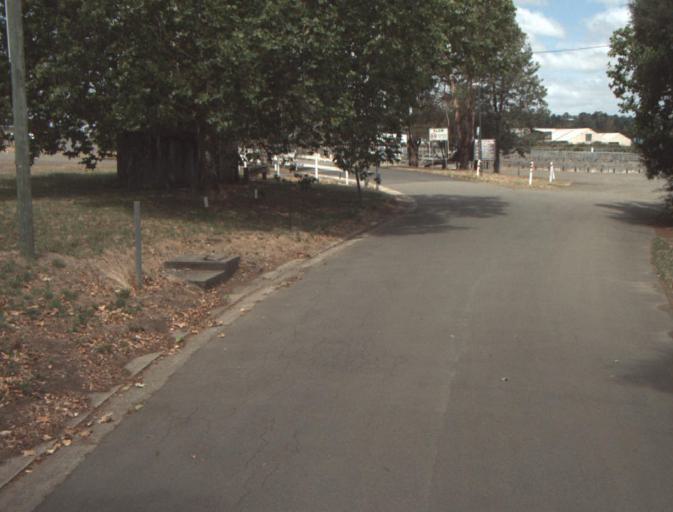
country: AU
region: Tasmania
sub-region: Launceston
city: Newstead
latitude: -41.4392
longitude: 147.1728
